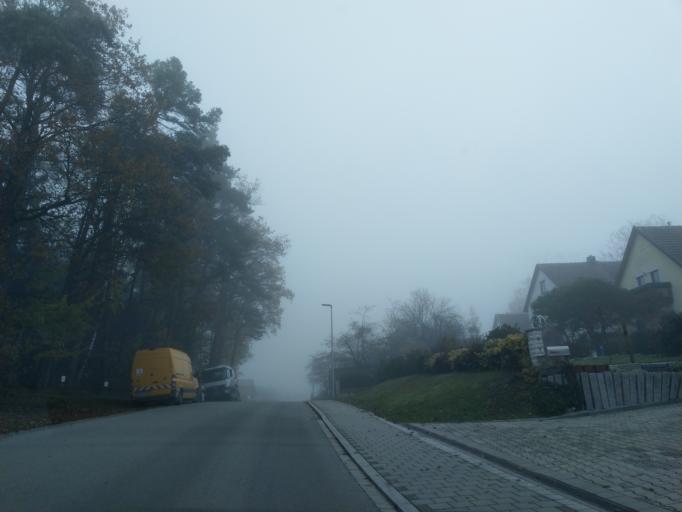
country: DE
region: Bavaria
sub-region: Lower Bavaria
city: Auerbach
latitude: 48.7802
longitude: 13.1086
